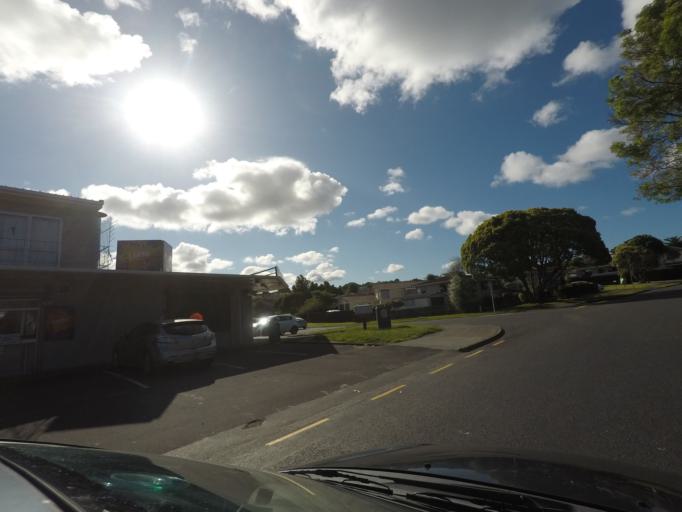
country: NZ
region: Auckland
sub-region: Auckland
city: Manukau City
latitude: -36.9862
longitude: 174.8896
